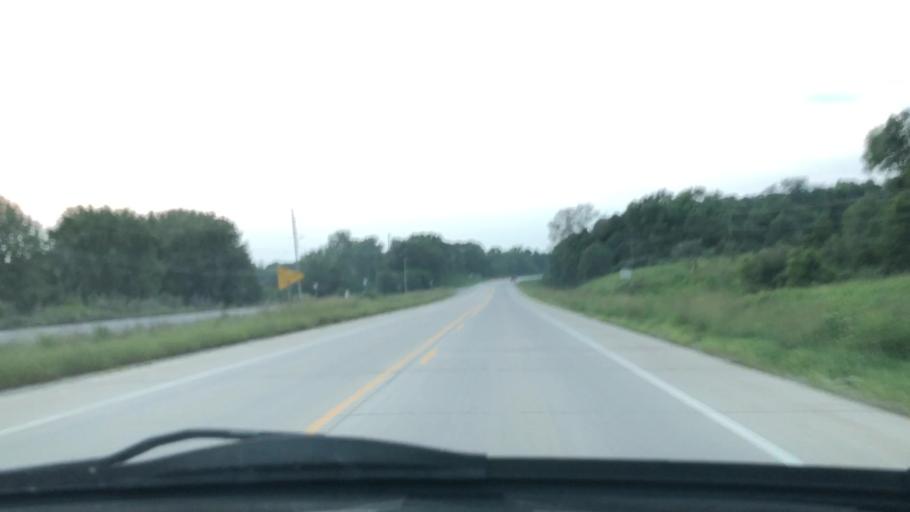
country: US
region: Iowa
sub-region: Johnson County
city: North Liberty
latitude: 41.8130
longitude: -91.6645
